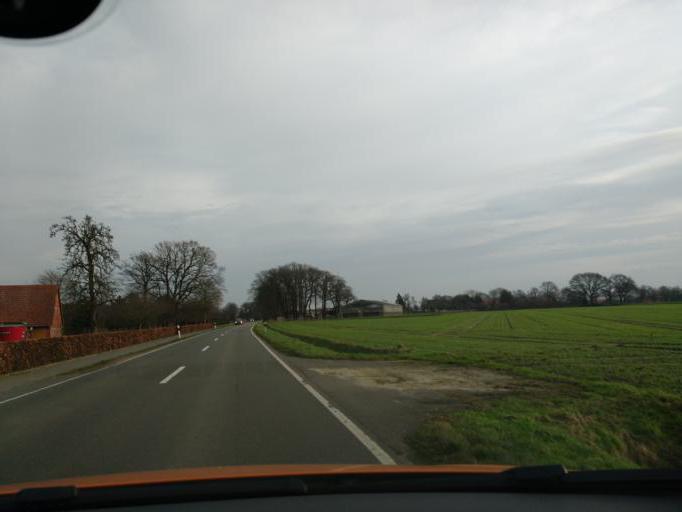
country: DE
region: Lower Saxony
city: Hatten
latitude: 53.0417
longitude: 8.4132
